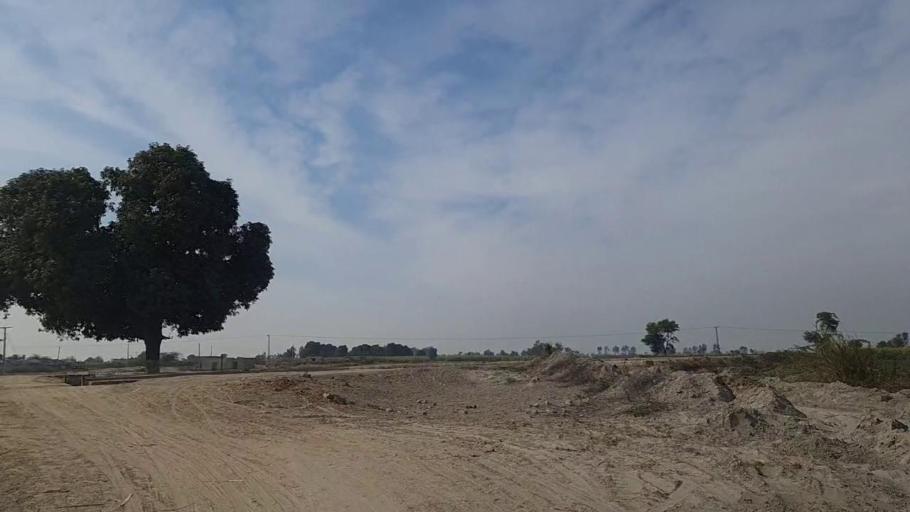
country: PK
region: Sindh
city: Nawabshah
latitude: 26.3283
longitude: 68.4198
